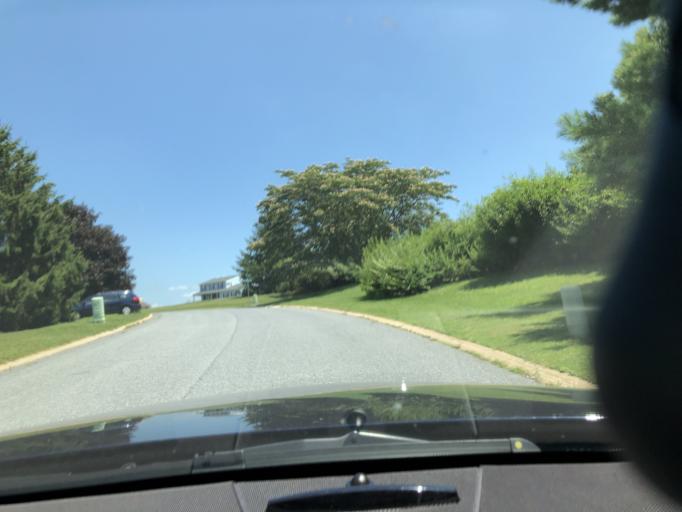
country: US
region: Maryland
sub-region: Carroll County
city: Westminster
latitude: 39.5521
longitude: -76.9658
